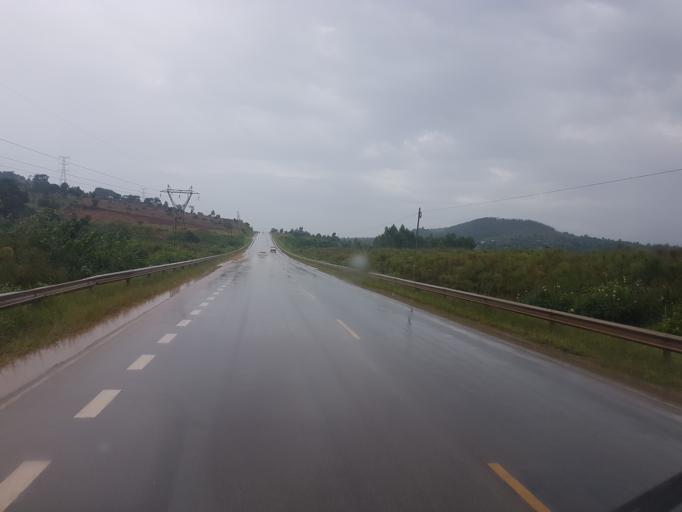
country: UG
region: Central Region
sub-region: Mpigi District
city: Mpigi
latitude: 0.1840
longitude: 32.2859
